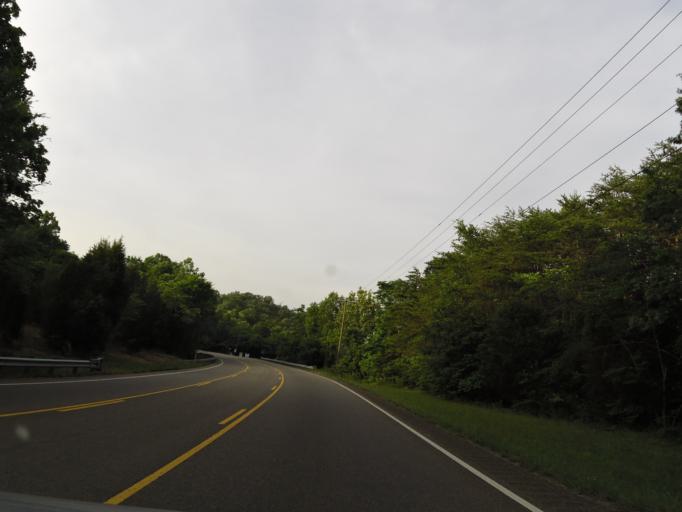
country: US
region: Tennessee
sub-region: Sevier County
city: Seymour
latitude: 35.9277
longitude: -83.8112
